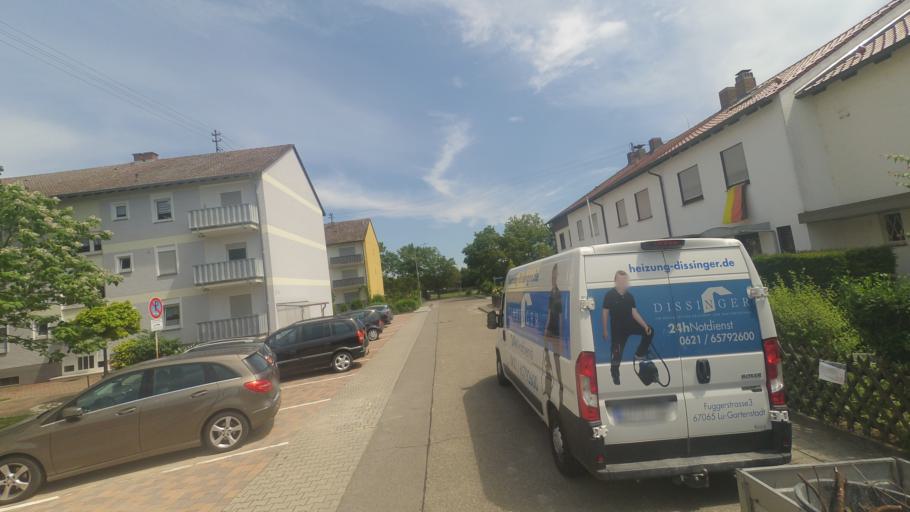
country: DE
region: Rheinland-Pfalz
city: Neuhofen
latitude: 49.4205
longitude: 8.4200
